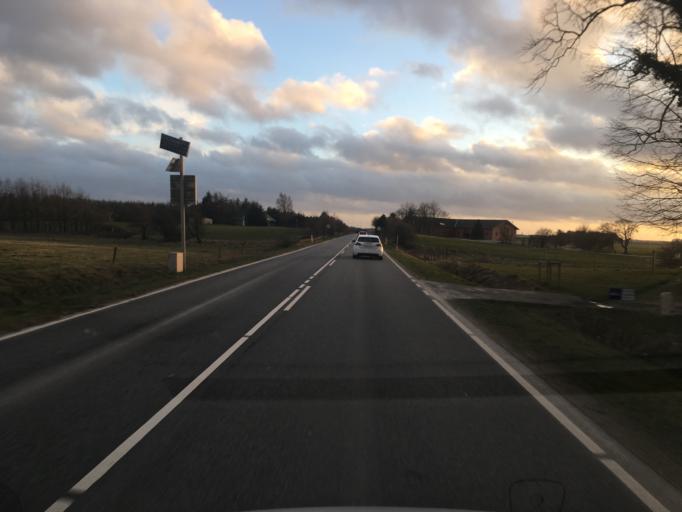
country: DK
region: South Denmark
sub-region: Aabenraa Kommune
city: Tinglev
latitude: 54.9537
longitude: 9.2803
